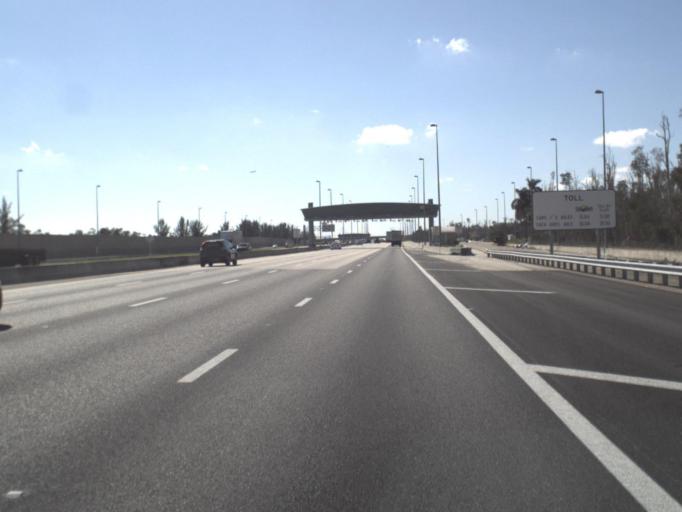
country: US
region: Florida
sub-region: Miami-Dade County
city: Doral
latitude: 25.8532
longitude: -80.3877
